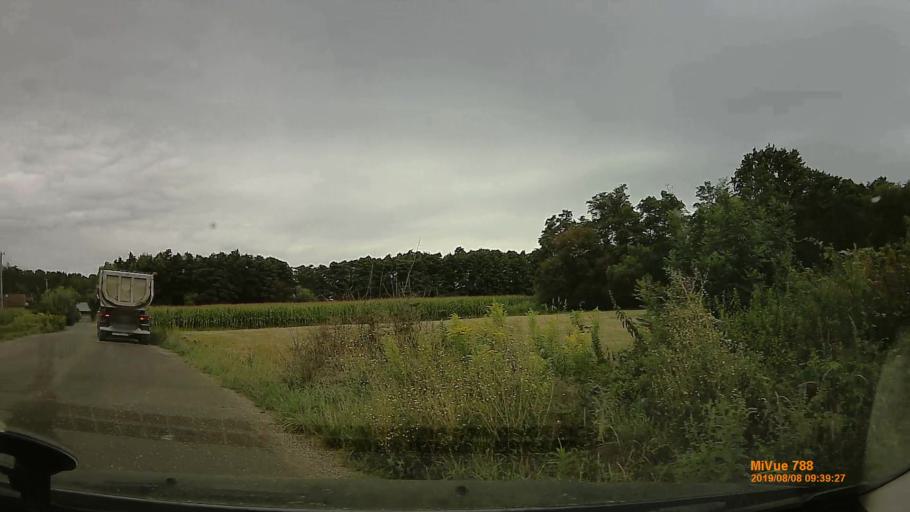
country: HU
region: Vas
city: Vasvar
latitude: 47.0573
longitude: 16.7903
